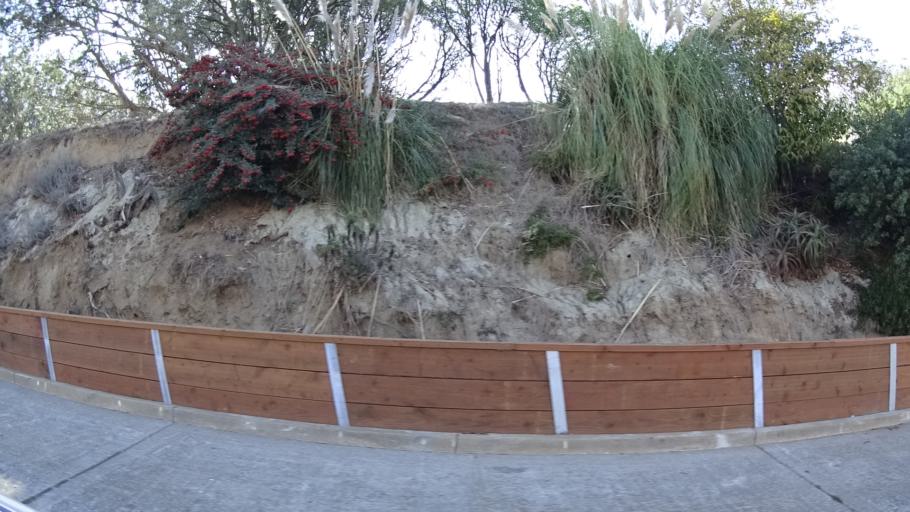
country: US
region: California
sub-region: San Mateo County
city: Brisbane
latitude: 37.7207
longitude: -122.4116
